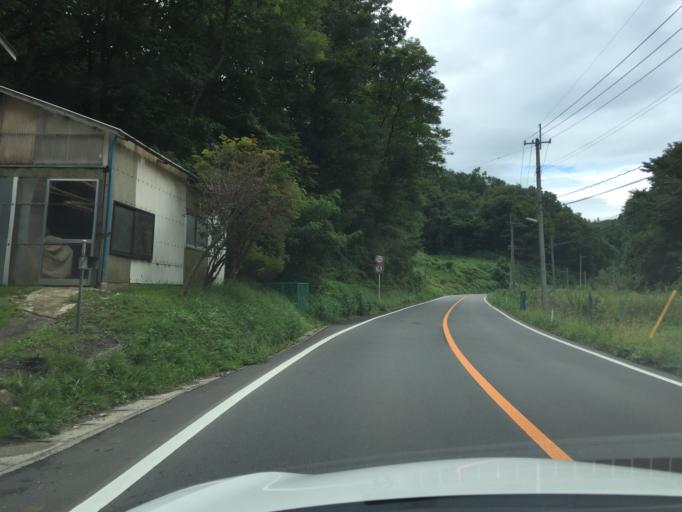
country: JP
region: Fukushima
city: Funehikimachi-funehiki
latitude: 37.4667
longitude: 140.5706
